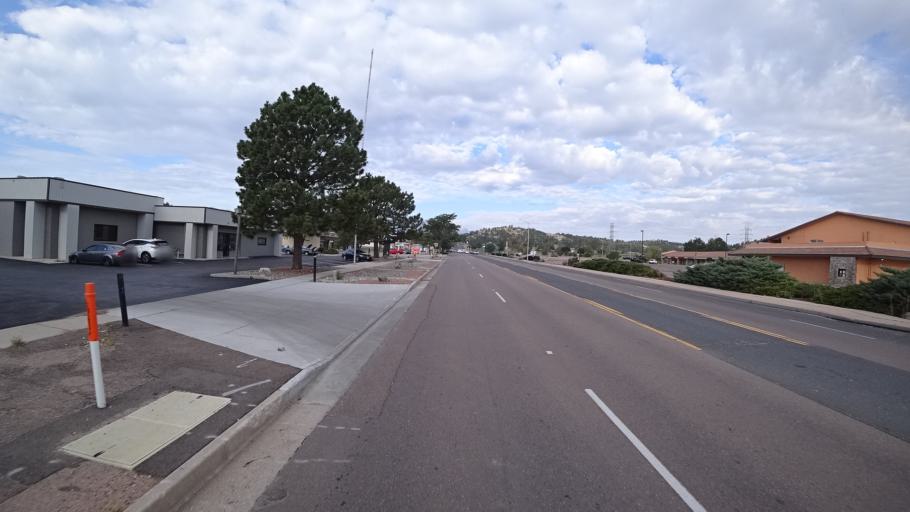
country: US
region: Colorado
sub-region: El Paso County
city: Cimarron Hills
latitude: 38.8678
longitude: -104.7546
